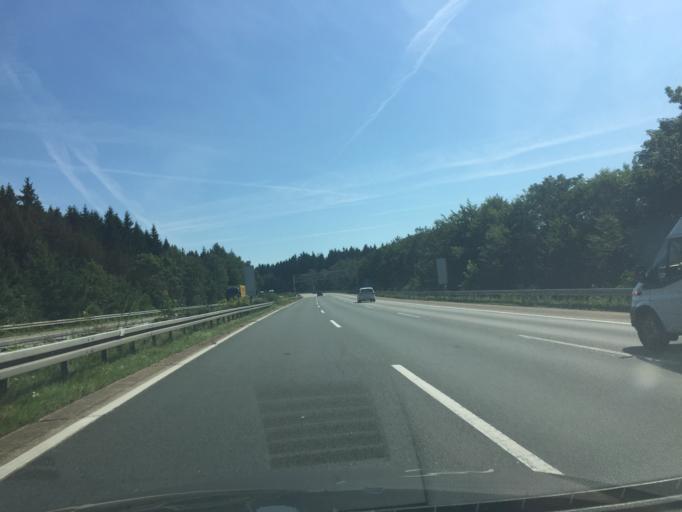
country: DE
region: North Rhine-Westphalia
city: Meinerzhagen
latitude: 51.1620
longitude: 7.6599
